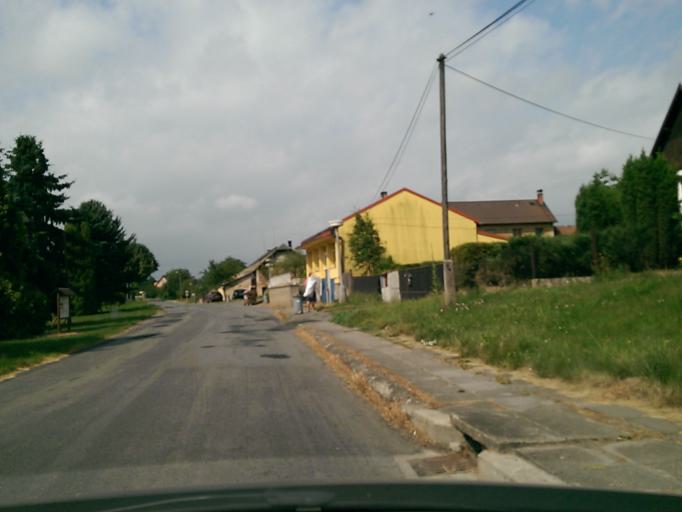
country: CZ
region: Central Bohemia
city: Bela pod Bezdezem
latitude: 50.4738
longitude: 14.8023
